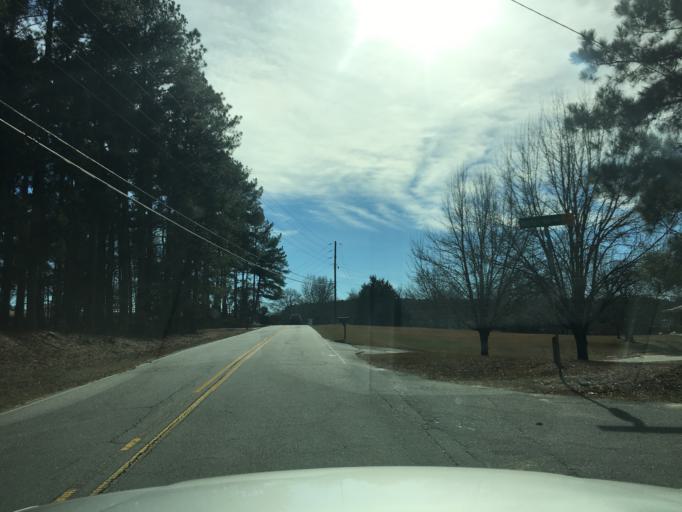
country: US
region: Georgia
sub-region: Rockdale County
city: Lakeview Estates
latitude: 33.7474
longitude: -84.0383
